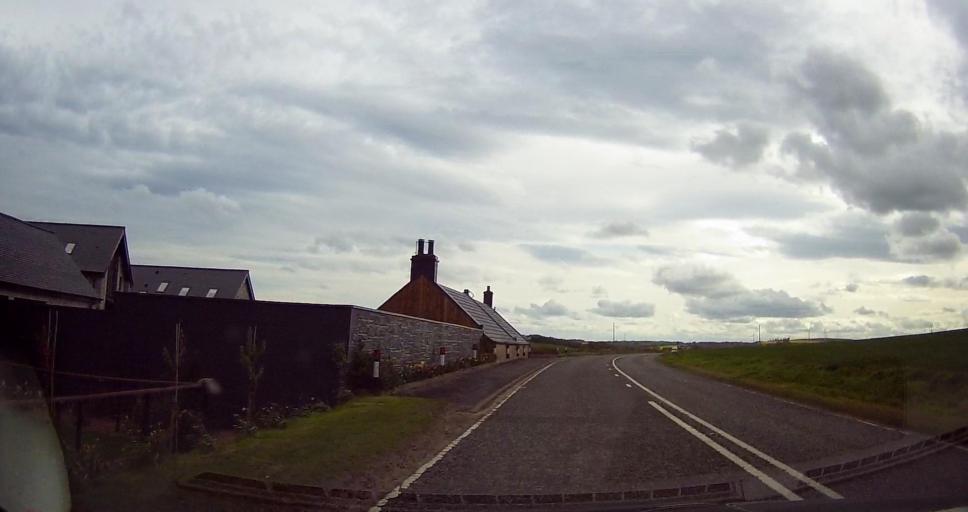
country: GB
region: Scotland
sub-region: Aberdeenshire
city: Stonehaven
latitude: 56.9172
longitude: -2.2126
